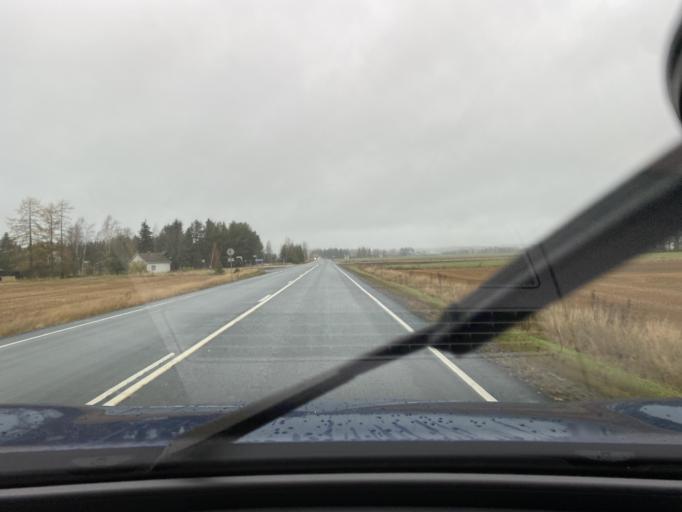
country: FI
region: Varsinais-Suomi
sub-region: Loimaa
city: Alastaro
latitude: 60.8863
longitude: 22.9729
